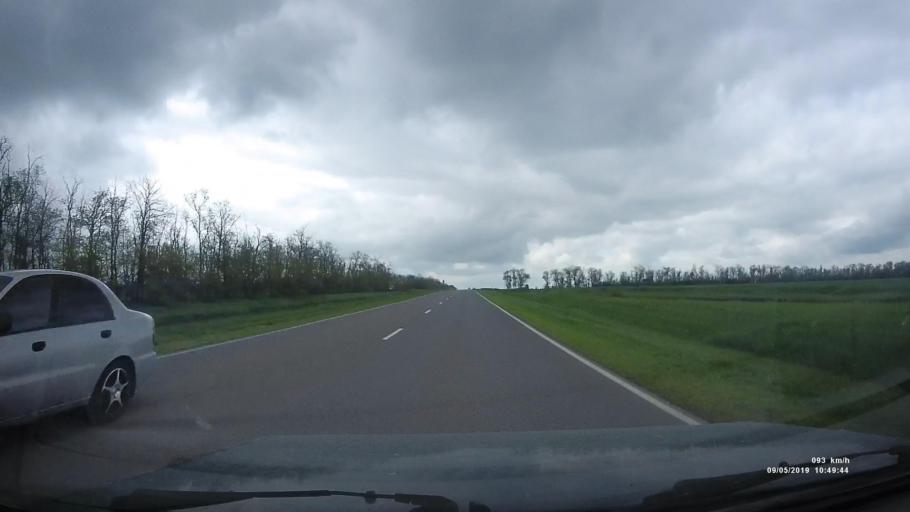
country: RU
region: Rostov
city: Peshkovo
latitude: 46.9383
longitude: 39.3554
